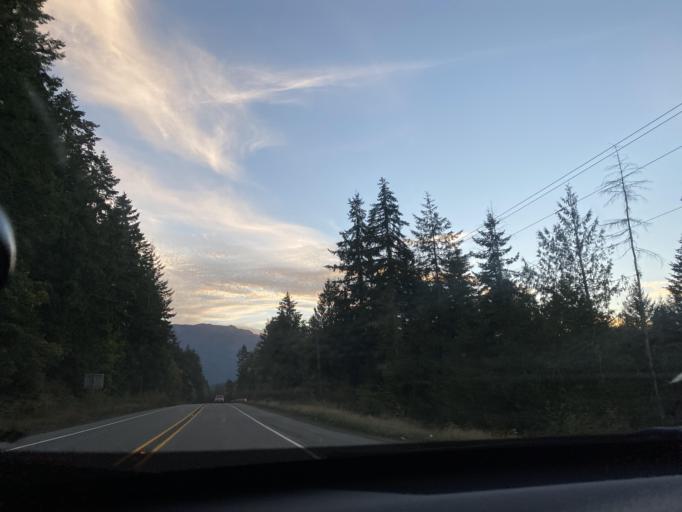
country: US
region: Washington
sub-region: Clallam County
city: Port Angeles
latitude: 48.0945
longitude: -123.5467
